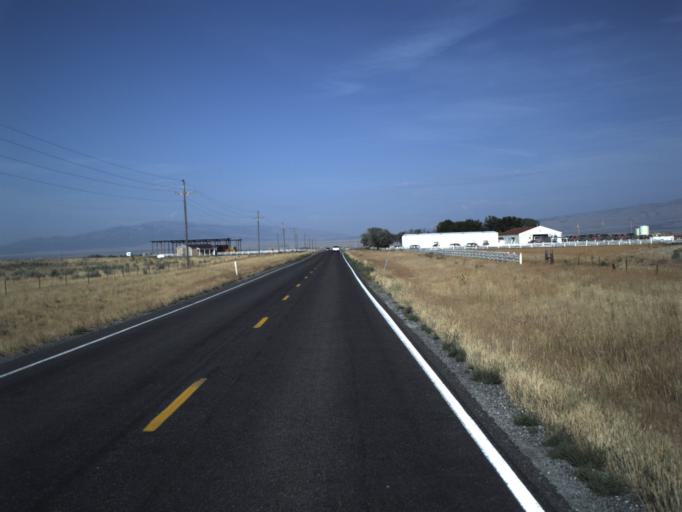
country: US
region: Idaho
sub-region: Oneida County
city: Malad City
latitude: 41.9672
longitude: -112.7998
